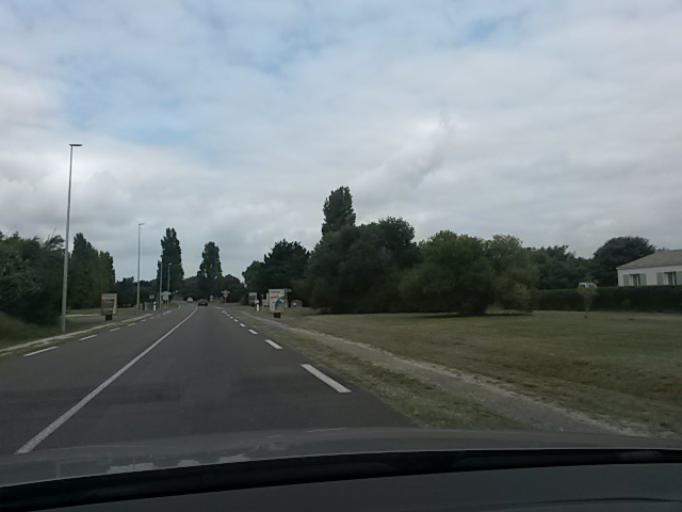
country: FR
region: Poitou-Charentes
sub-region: Departement de la Charente-Maritime
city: Saint-Trojan-les-Bains
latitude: 45.8635
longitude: -1.2341
